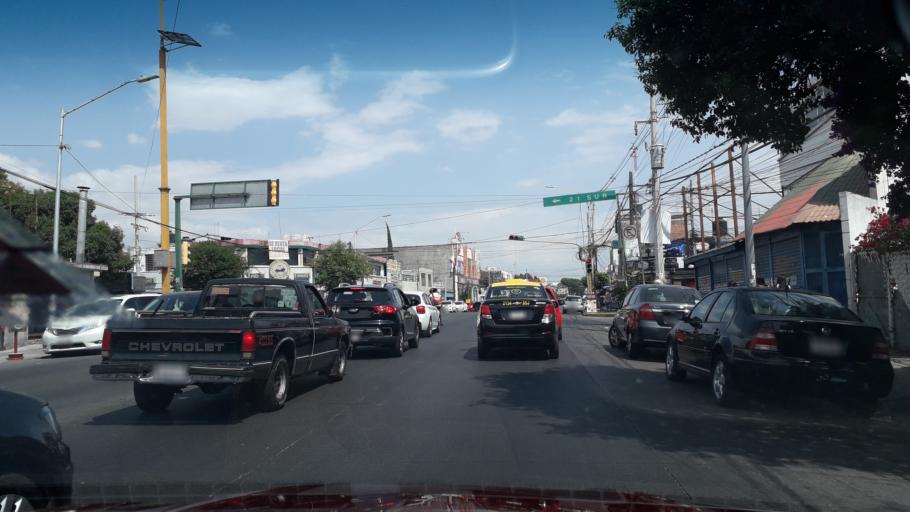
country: MX
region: Puebla
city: Puebla
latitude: 19.0405
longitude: -98.2206
